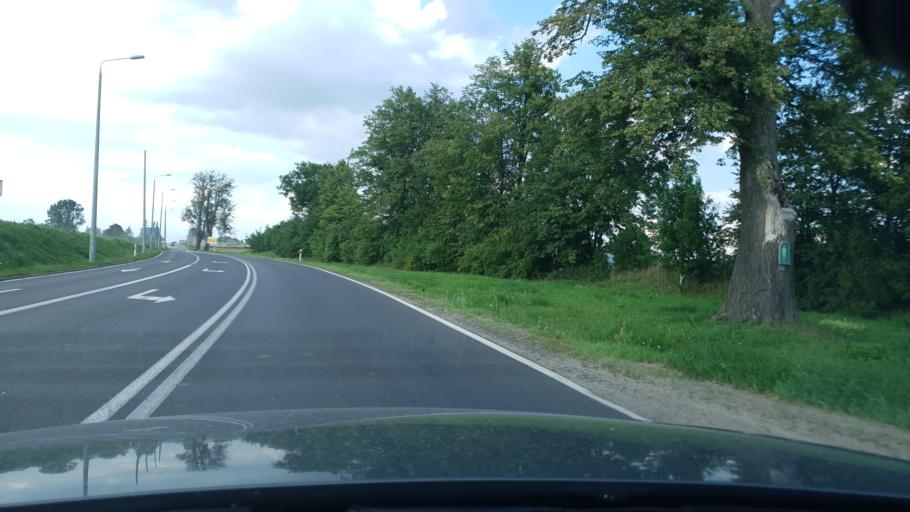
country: PL
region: Kujawsko-Pomorskie
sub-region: Powiat wabrzeski
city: Wabrzezno
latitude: 53.3077
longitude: 18.9346
